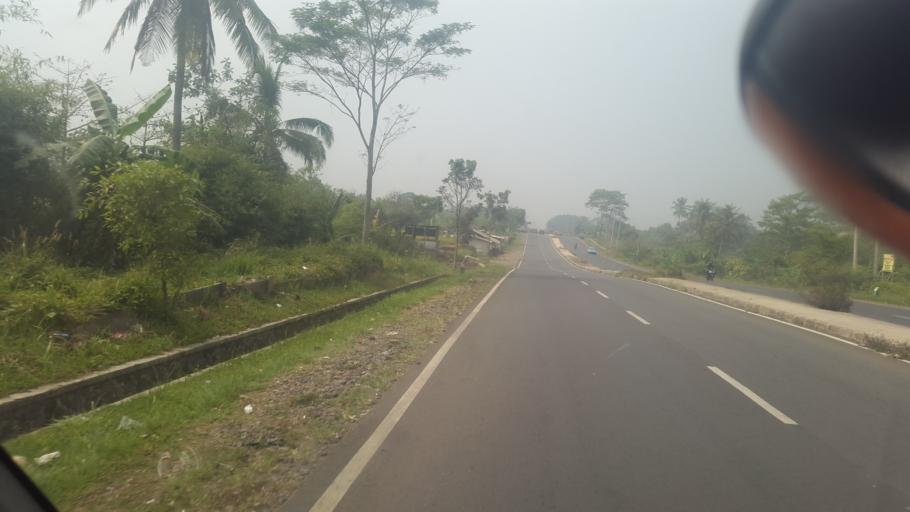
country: ID
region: West Java
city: Sukabumi
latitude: -6.9266
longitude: 106.8963
